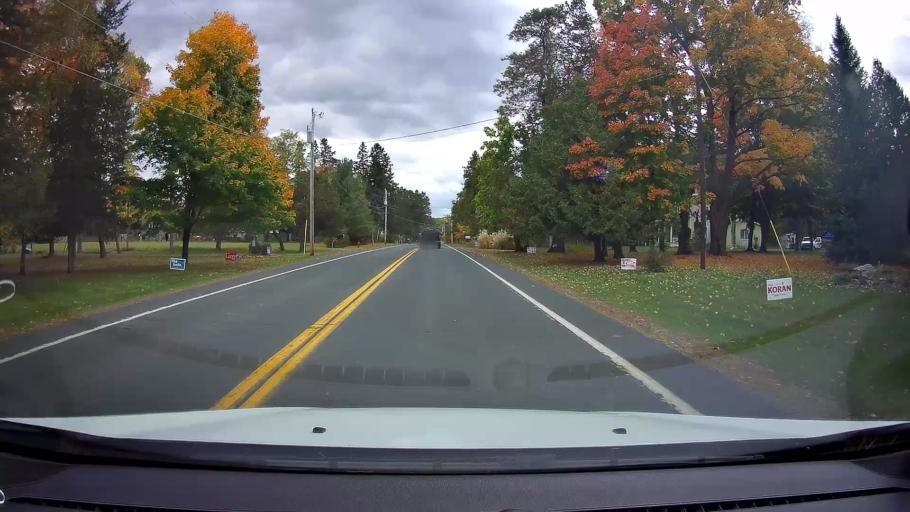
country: US
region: Wisconsin
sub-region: Polk County
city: Saint Croix Falls
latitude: 45.4160
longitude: -92.6621
